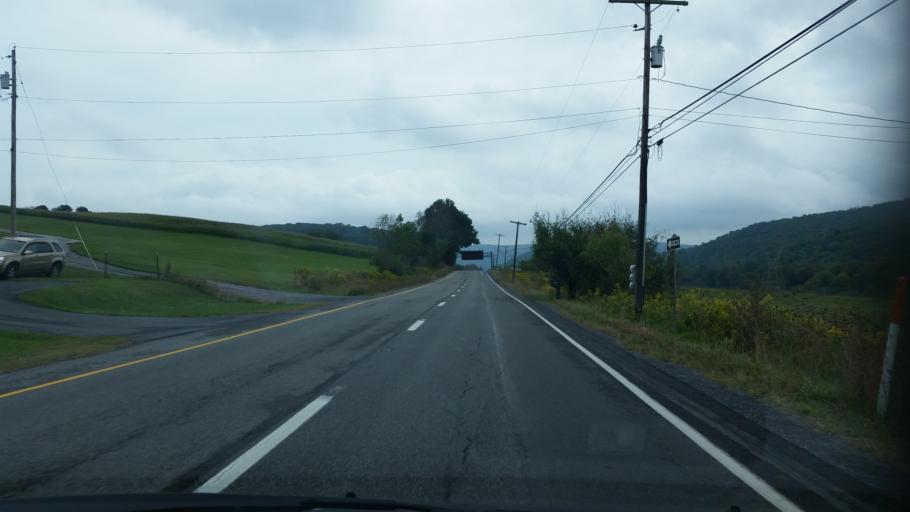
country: US
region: Pennsylvania
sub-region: Centre County
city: Stormstown
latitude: 40.8190
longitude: -78.0962
